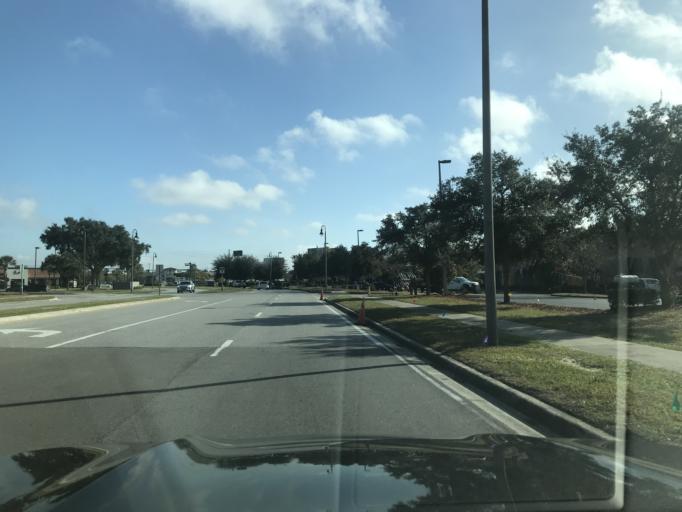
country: US
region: Florida
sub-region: Polk County
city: Citrus Ridge
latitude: 28.3392
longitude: -81.5990
